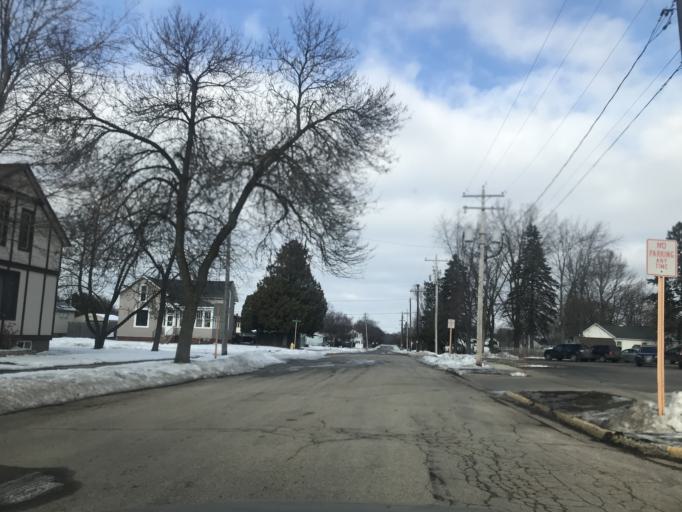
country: US
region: Wisconsin
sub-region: Marinette County
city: Marinette
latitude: 45.1000
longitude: -87.6413
